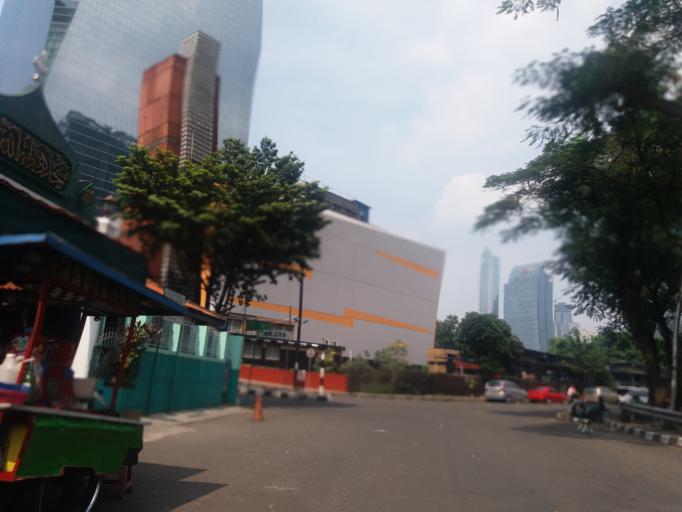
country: ID
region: Jakarta Raya
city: Jakarta
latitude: -6.2177
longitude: 106.8175
